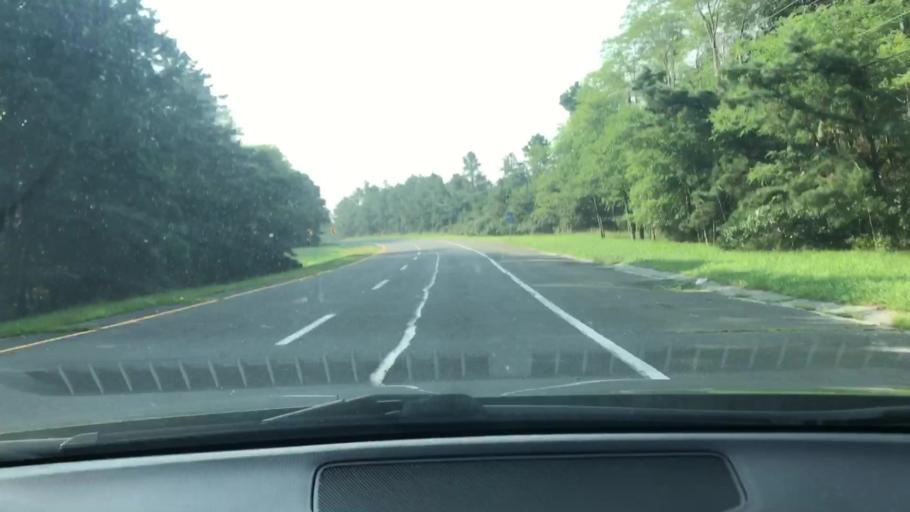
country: US
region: New York
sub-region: Suffolk County
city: Riverhead
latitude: 40.8996
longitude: -72.6509
